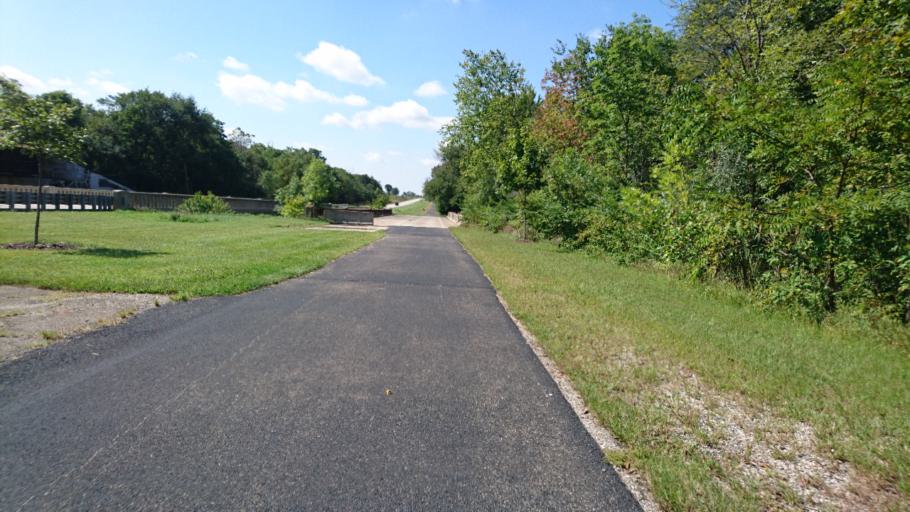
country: US
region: Illinois
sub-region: McLean County
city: Lexington
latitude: 40.6326
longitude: -88.7991
